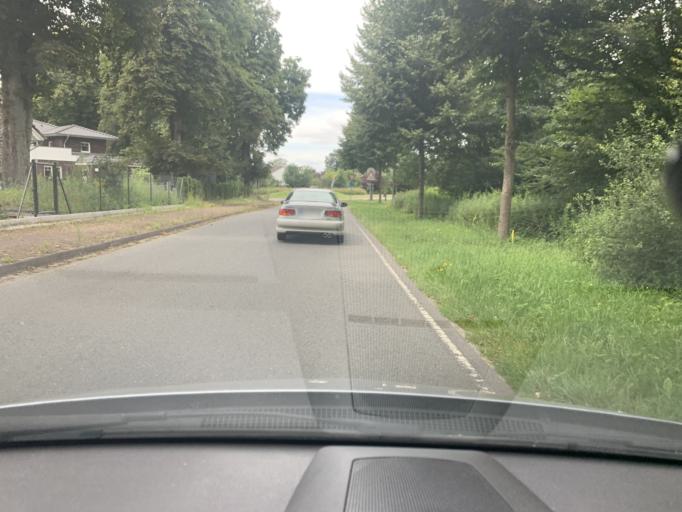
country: DE
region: Schleswig-Holstein
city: Grambek
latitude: 53.5712
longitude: 10.6831
